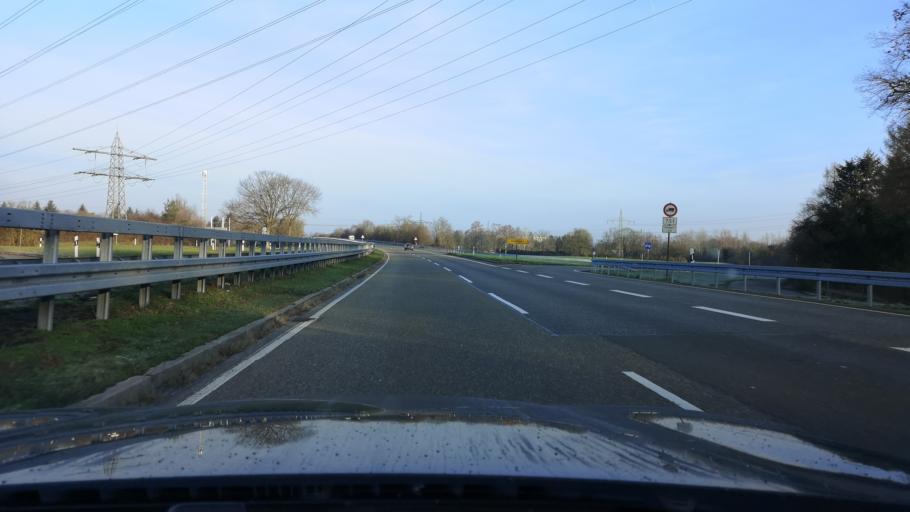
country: DE
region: Baden-Wuerttemberg
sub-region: Karlsruhe Region
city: Karlsruhe
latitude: 48.9747
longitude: 8.3759
